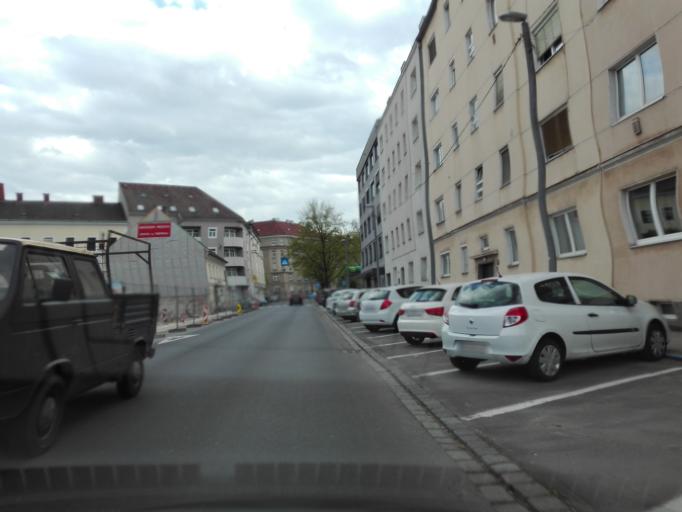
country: AT
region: Upper Austria
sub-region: Linz Stadt
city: Linz
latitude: 48.2942
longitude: 14.2857
